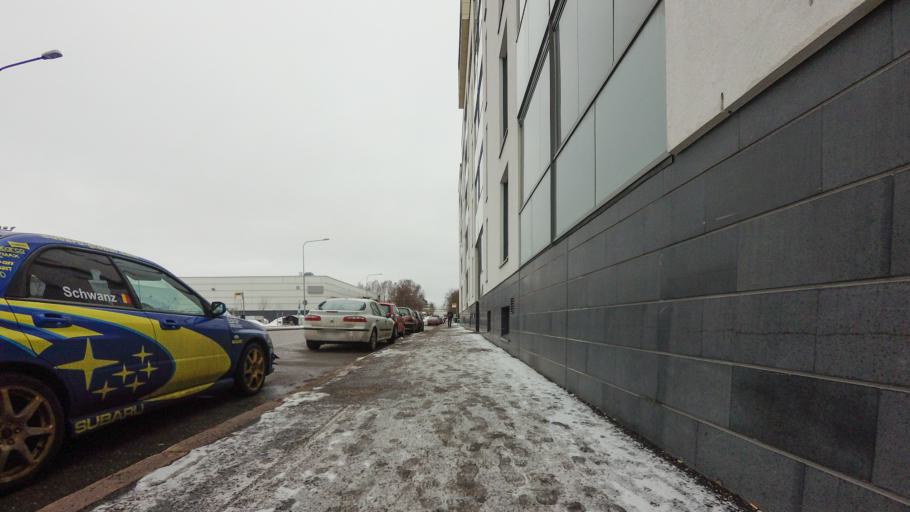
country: FI
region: Uusimaa
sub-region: Helsinki
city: Vantaa
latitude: 60.1933
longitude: 25.0428
